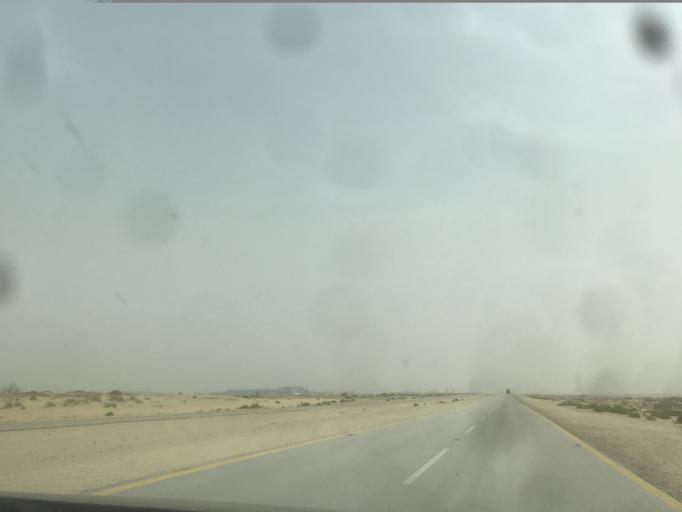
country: SA
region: Eastern Province
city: Abqaiq
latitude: 25.9094
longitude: 49.9391
